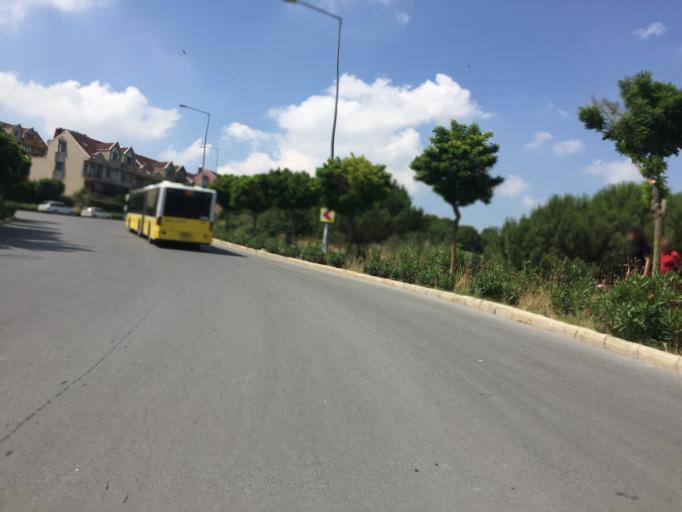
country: TR
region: Istanbul
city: Esenyurt
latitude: 41.0835
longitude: 28.6692
